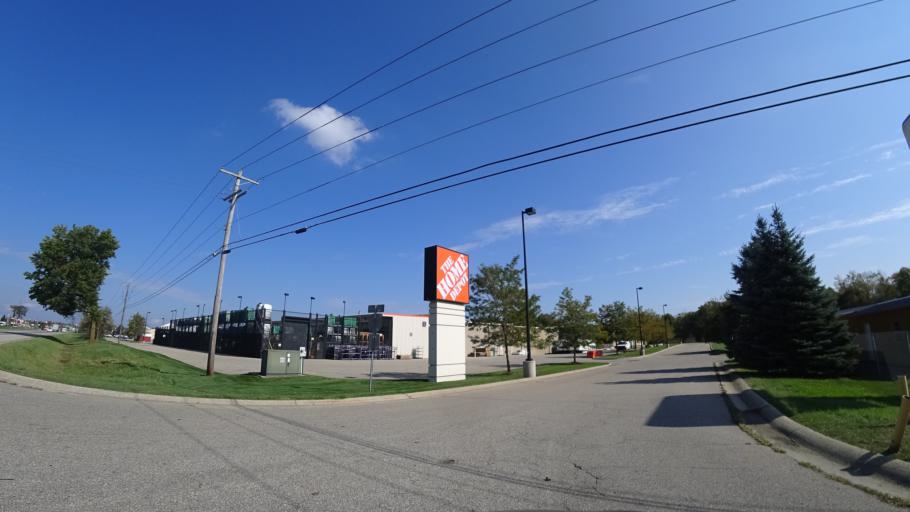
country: US
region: Michigan
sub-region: Saint Joseph County
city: Three Rivers
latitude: 41.9294
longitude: -85.6513
